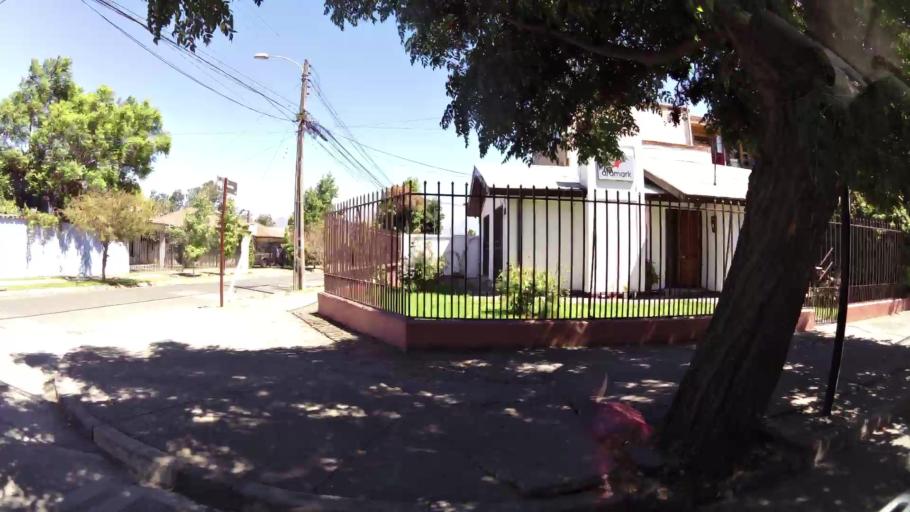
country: CL
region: O'Higgins
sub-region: Provincia de Cachapoal
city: Rancagua
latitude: -34.1618
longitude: -70.7475
